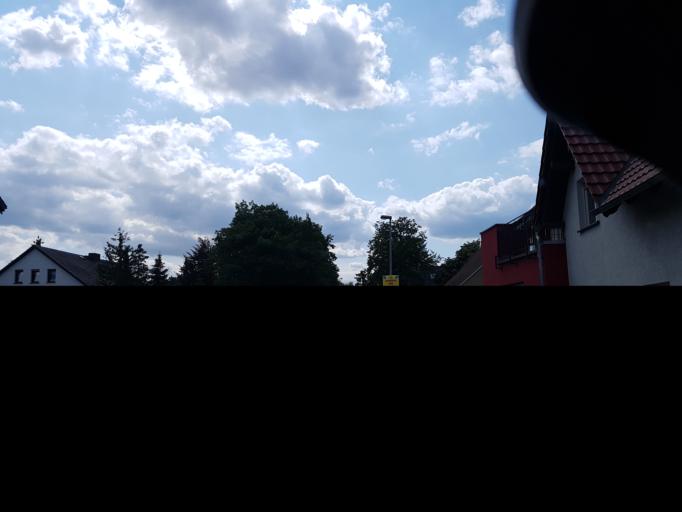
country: DE
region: Brandenburg
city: Cottbus
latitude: 51.7220
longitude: 14.3630
